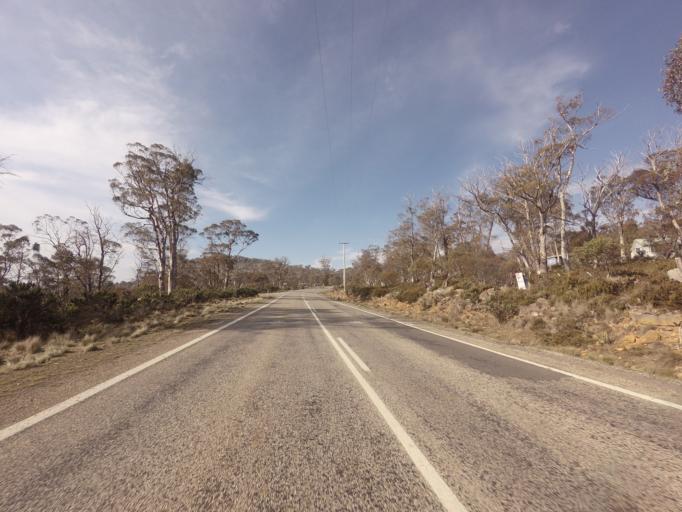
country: AU
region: Tasmania
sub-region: Meander Valley
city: Deloraine
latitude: -41.9905
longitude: 146.6899
